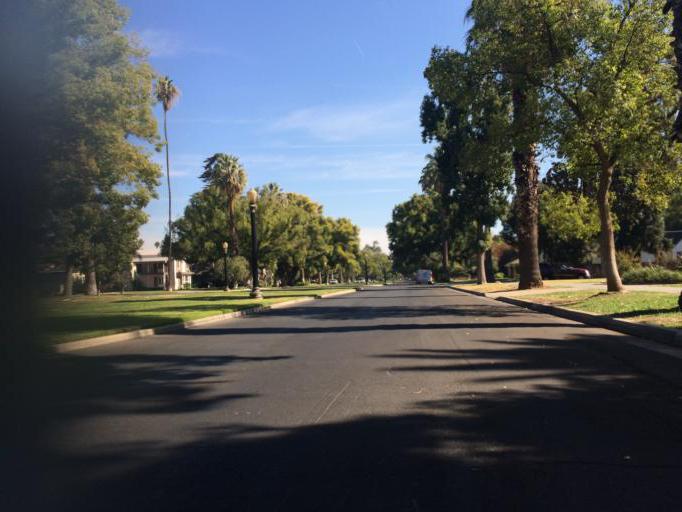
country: US
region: California
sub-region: Fresno County
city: Fresno
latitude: 36.7393
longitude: -119.7701
